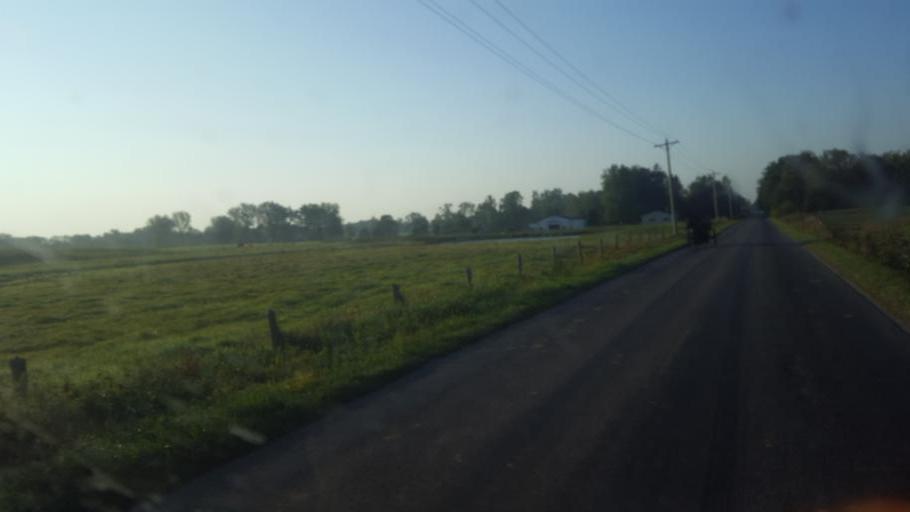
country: US
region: Indiana
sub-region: LaGrange County
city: Lagrange
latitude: 41.5956
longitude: -85.4242
